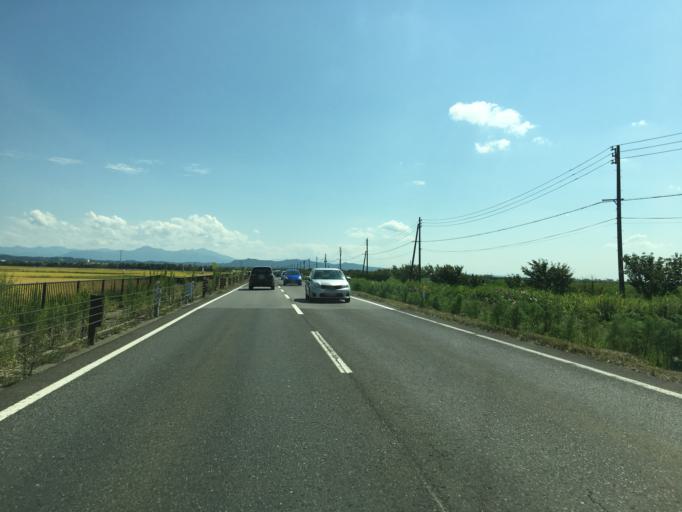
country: JP
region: Niigata
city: Niitsu-honcho
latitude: 37.8303
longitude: 139.0973
